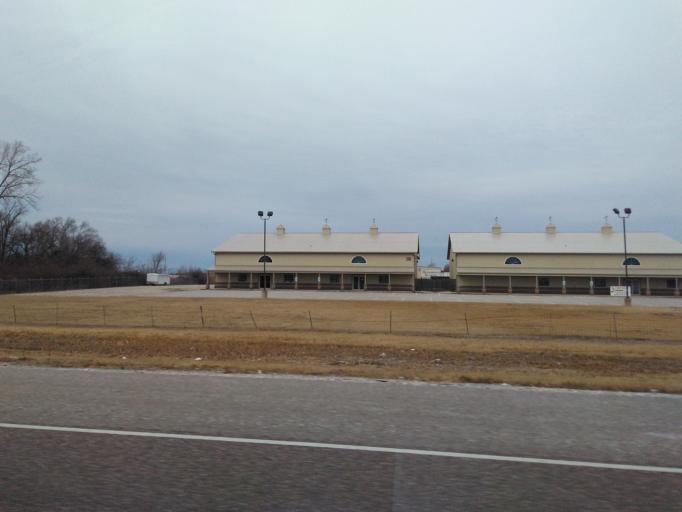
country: US
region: Illinois
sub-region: Saint Clair County
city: Washington Park
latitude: 38.6190
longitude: -90.0594
